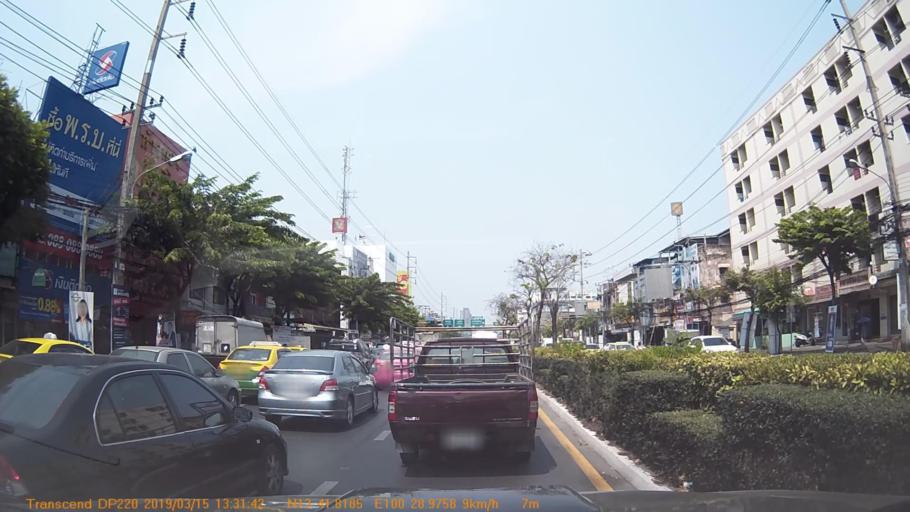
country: TH
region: Bangkok
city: Bang Kho Laem
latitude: 13.6970
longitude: 100.4829
